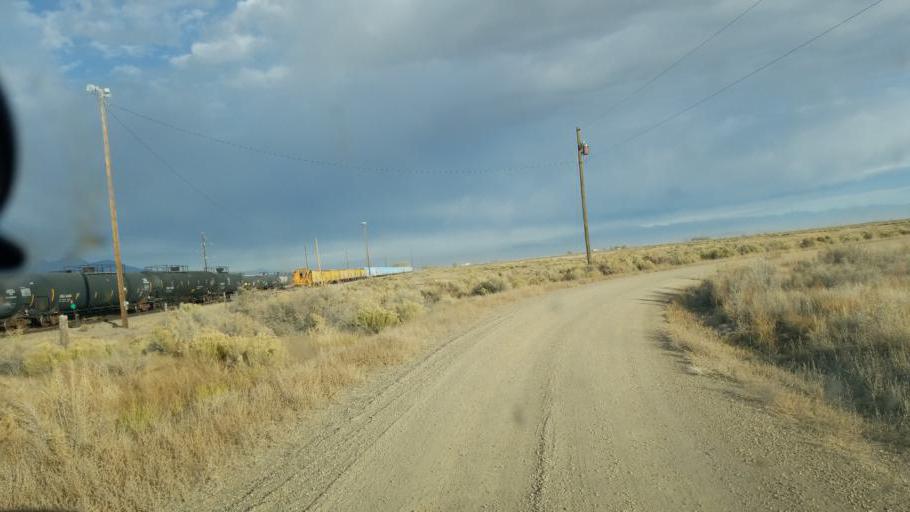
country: US
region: Colorado
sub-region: Alamosa County
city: Alamosa East
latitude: 37.4650
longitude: -105.8348
